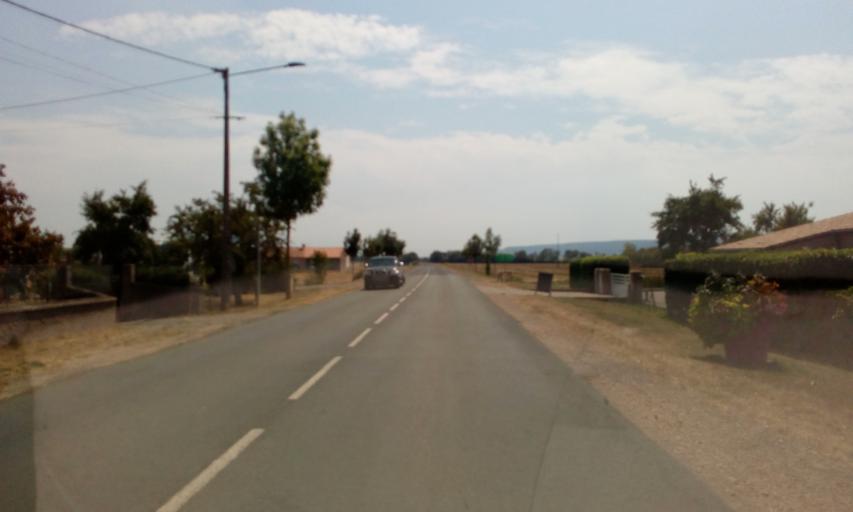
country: FR
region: Lorraine
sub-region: Departement de la Meuse
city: Etain
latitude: 49.0917
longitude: 5.6274
